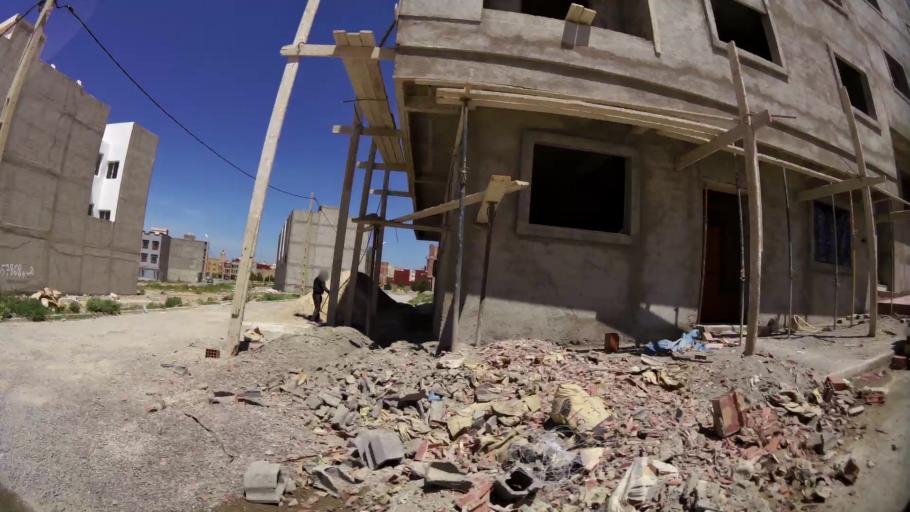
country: MA
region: Oriental
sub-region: Oujda-Angad
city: Oujda
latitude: 34.6541
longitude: -1.9220
